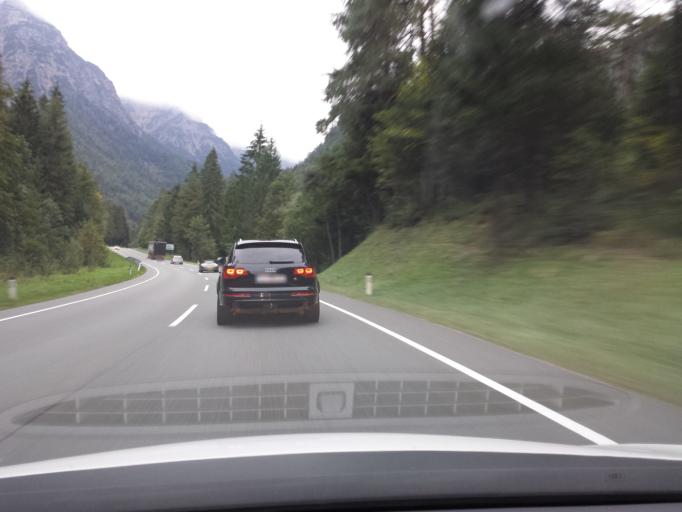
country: AT
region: Salzburg
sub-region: Politischer Bezirk Zell am See
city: Sankt Martin bei Lofer
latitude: 47.5440
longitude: 12.7197
